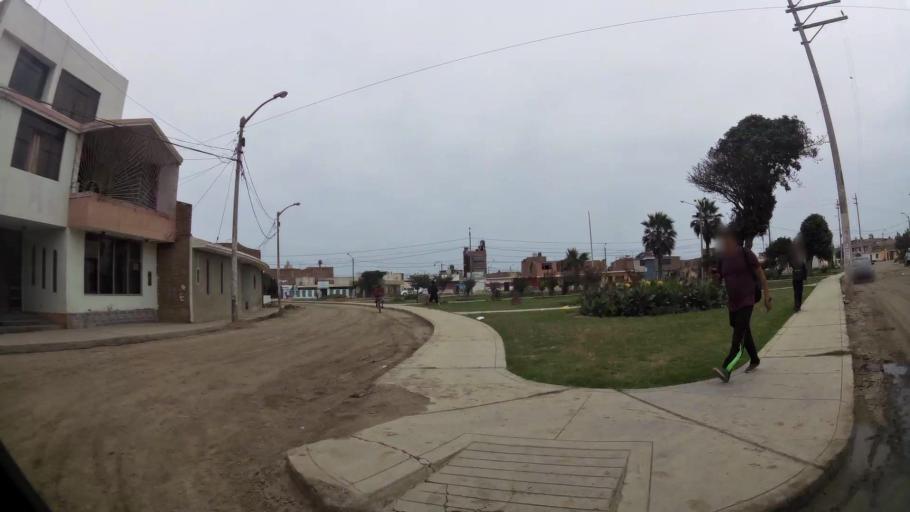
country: PE
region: La Libertad
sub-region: Provincia de Trujillo
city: Buenos Aires
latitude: -8.1414
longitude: -79.0507
